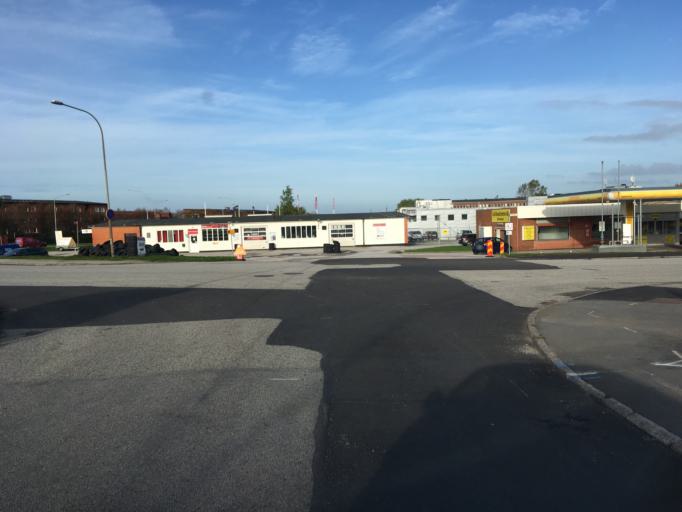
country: SE
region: Skane
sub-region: Lunds Kommun
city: Lund
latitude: 55.7118
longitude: 13.1707
